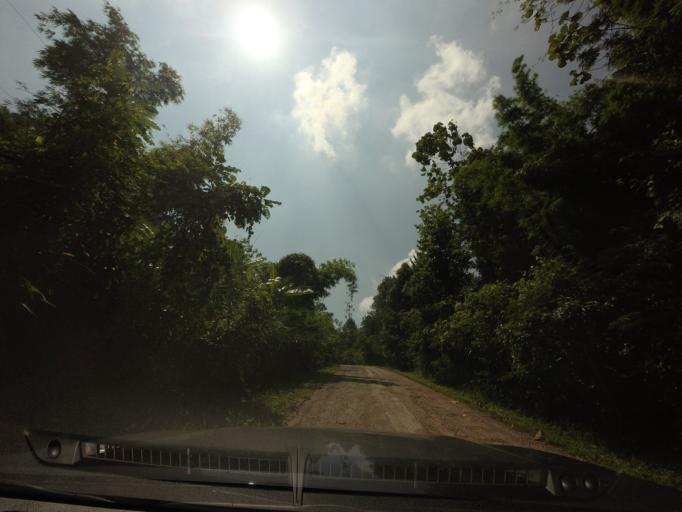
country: TH
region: Loei
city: Na Haeo
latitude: 17.5278
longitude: 100.9379
